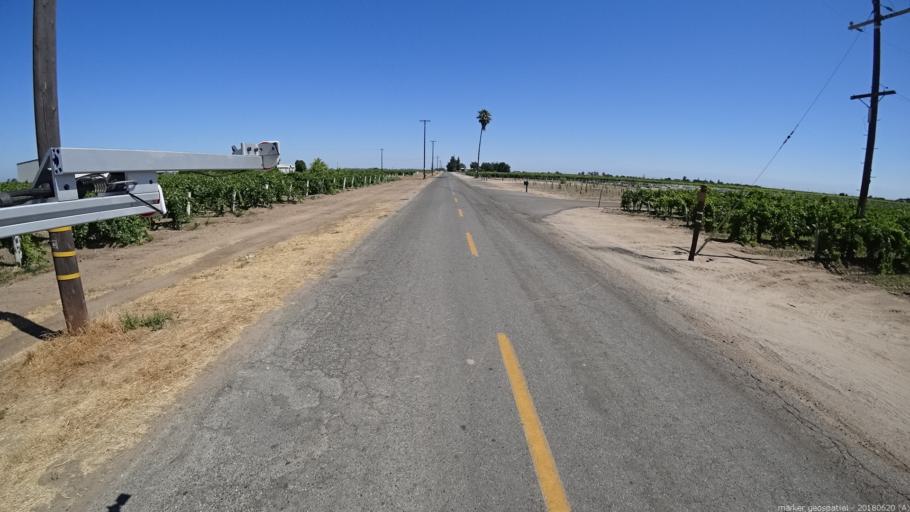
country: US
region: California
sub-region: Fresno County
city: Biola
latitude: 36.8550
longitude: -120.0193
